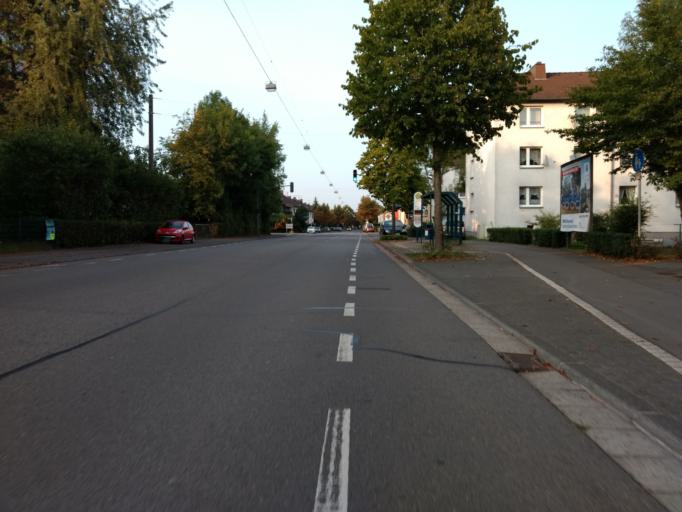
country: DE
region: Saarland
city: Wallerfangen
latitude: 49.3444
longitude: 6.7216
